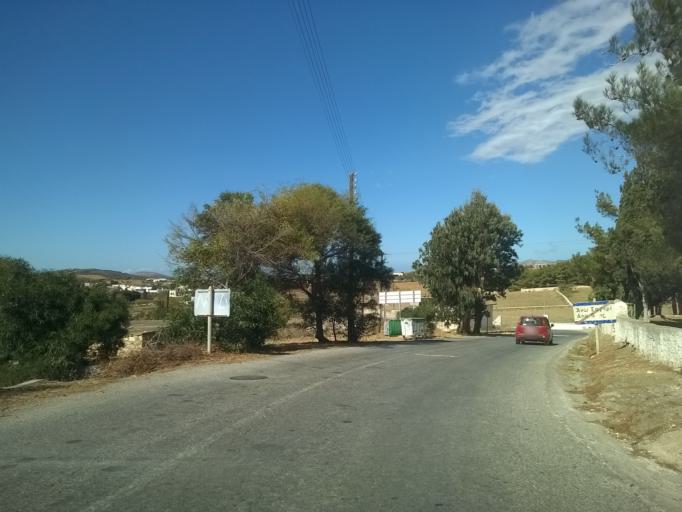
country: GR
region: South Aegean
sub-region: Nomos Kykladon
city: Filotion
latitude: 37.0425
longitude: 25.4357
